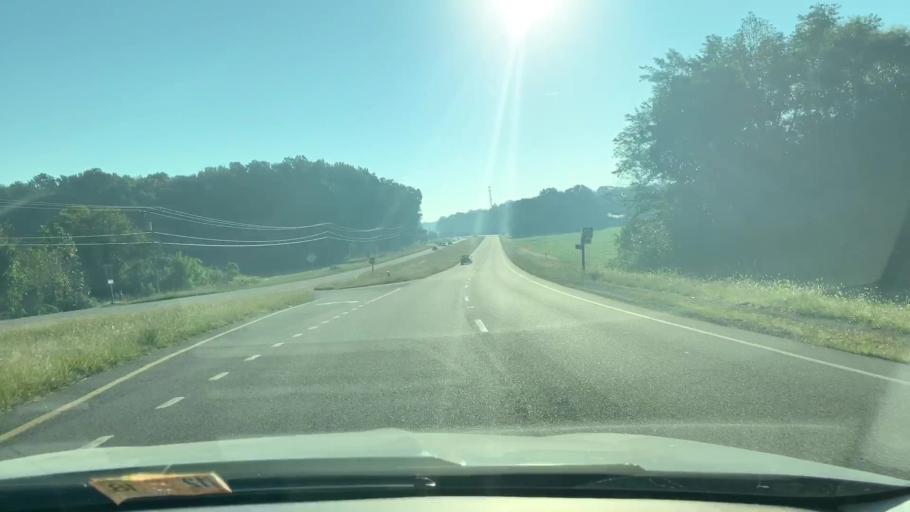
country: US
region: Virginia
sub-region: Gloucester County
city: Gloucester Courthouse
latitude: 37.4664
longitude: -76.4557
